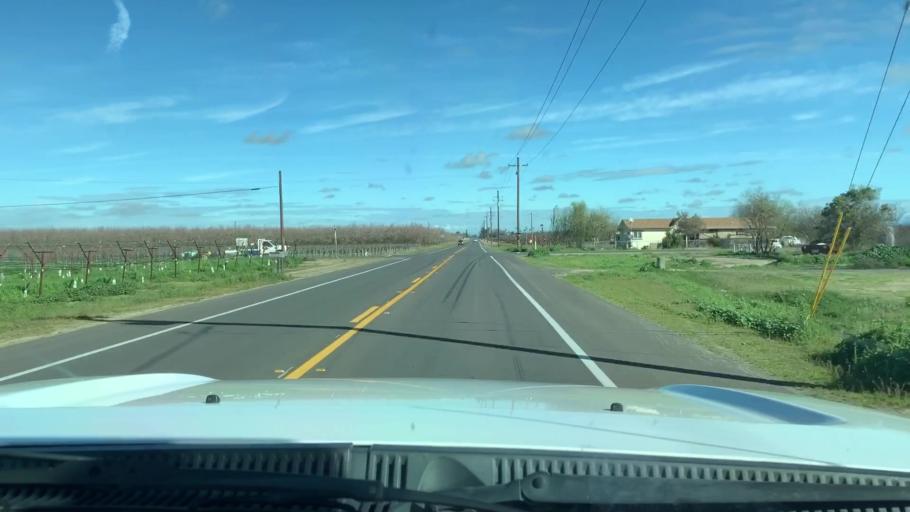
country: US
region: California
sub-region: Fresno County
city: Laton
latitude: 36.5176
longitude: -119.6829
